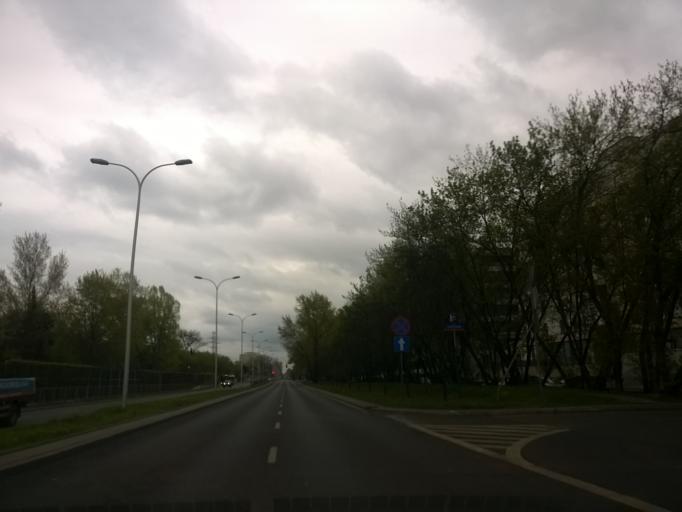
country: PL
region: Masovian Voivodeship
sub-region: Warszawa
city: Ursynow
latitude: 52.1732
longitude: 21.0523
